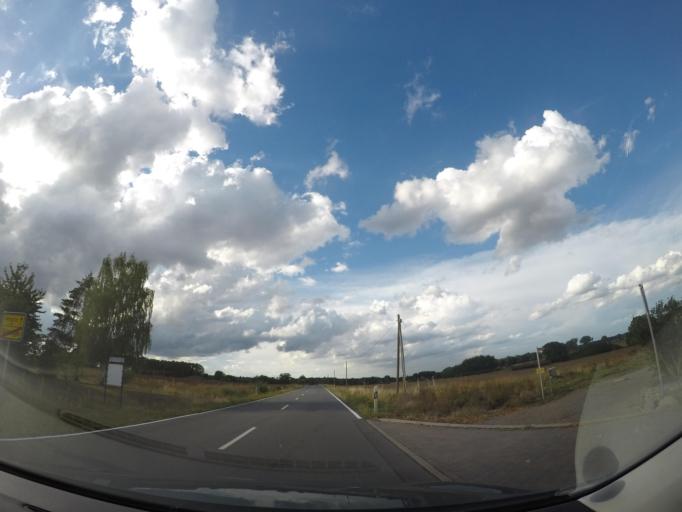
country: DE
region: Saxony-Anhalt
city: Bulstringen
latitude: 52.3229
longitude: 11.3414
